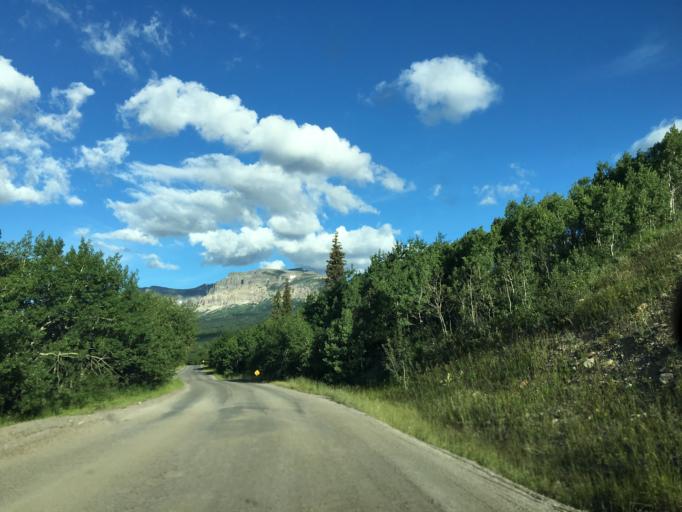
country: CA
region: Alberta
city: Cardston
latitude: 48.8300
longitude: -113.5264
